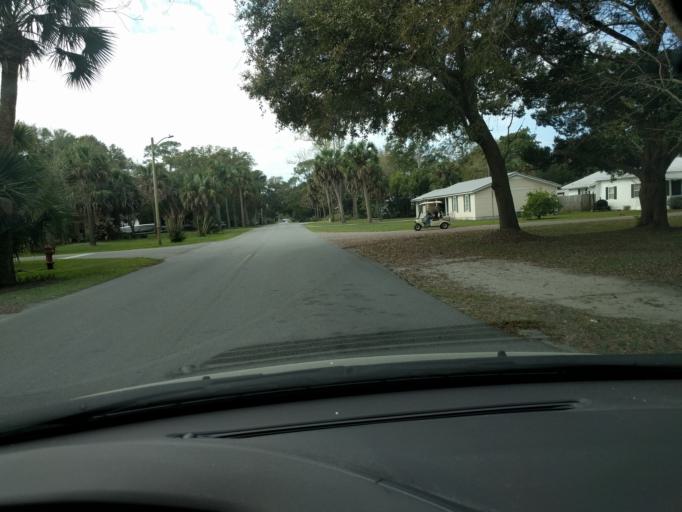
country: US
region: Florida
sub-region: Franklin County
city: Apalachicola
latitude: 29.7221
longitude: -84.9888
